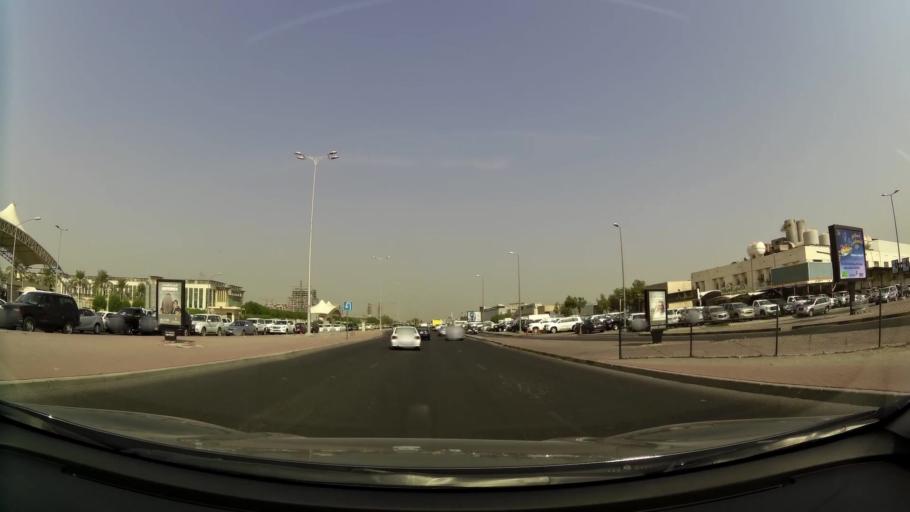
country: KW
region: Al Asimah
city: Ar Rabiyah
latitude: 29.3030
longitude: 47.9274
